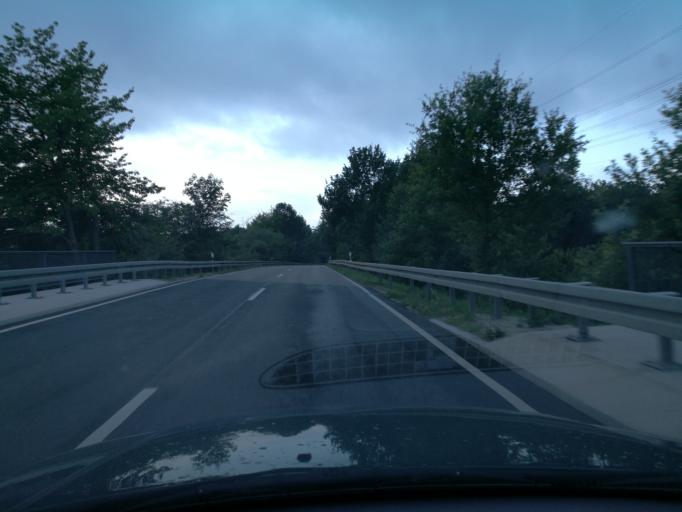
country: DE
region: Bavaria
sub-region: Regierungsbezirk Mittelfranken
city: Obermichelbach
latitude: 49.5602
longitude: 10.9550
